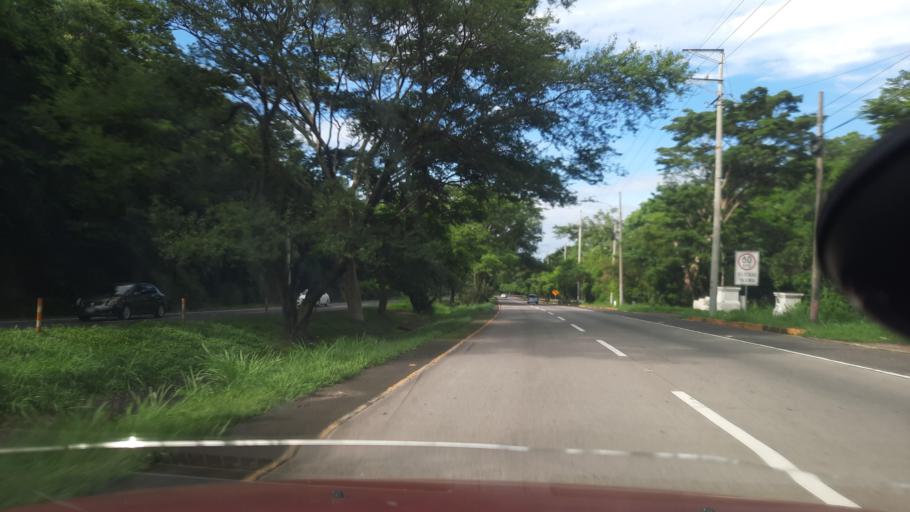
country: SV
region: La Paz
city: Olocuilta
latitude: 13.5334
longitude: -89.1129
